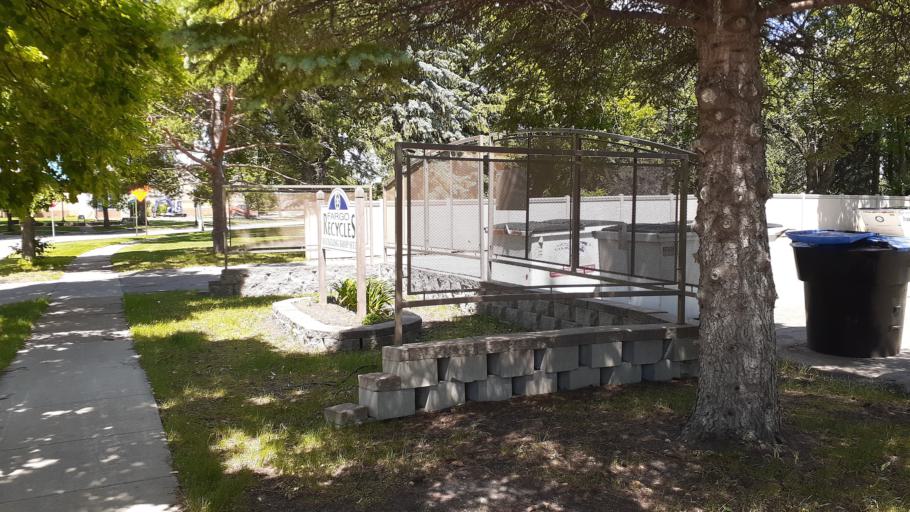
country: US
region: North Dakota
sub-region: Cass County
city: Fargo
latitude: 46.8593
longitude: -96.7842
